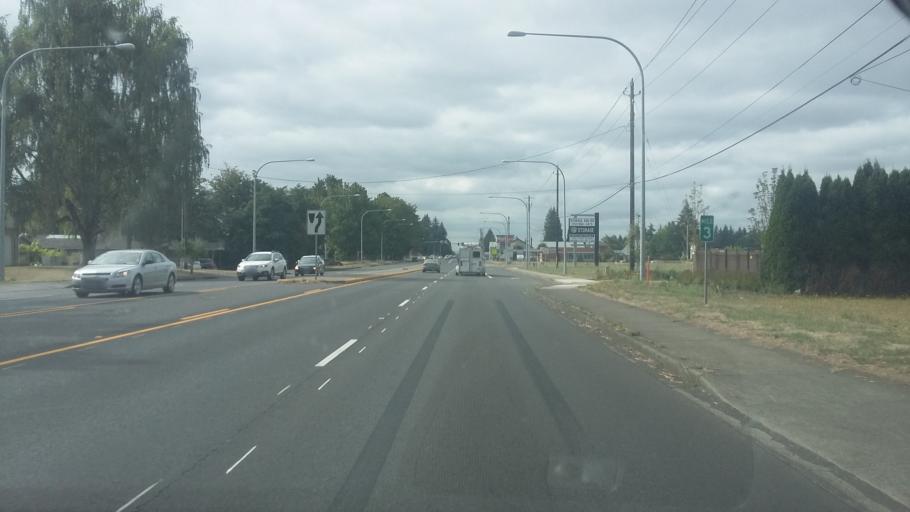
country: US
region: Washington
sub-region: Clark County
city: Brush Prairie
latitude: 45.7112
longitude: -122.5528
